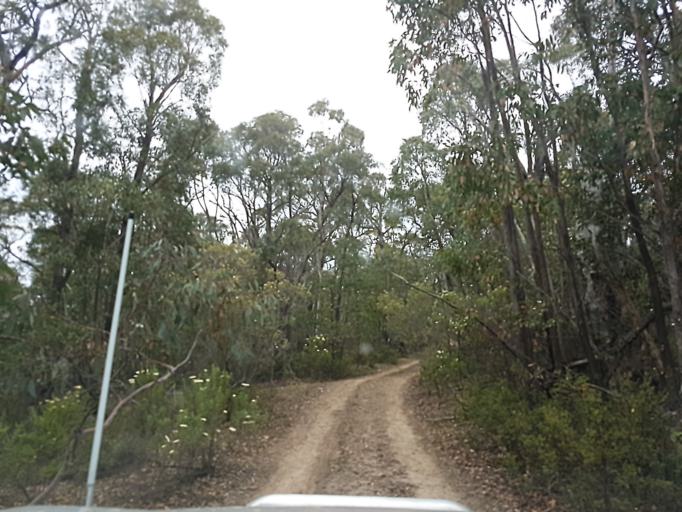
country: AU
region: New South Wales
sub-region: Snowy River
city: Jindabyne
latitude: -36.8646
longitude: 148.2655
